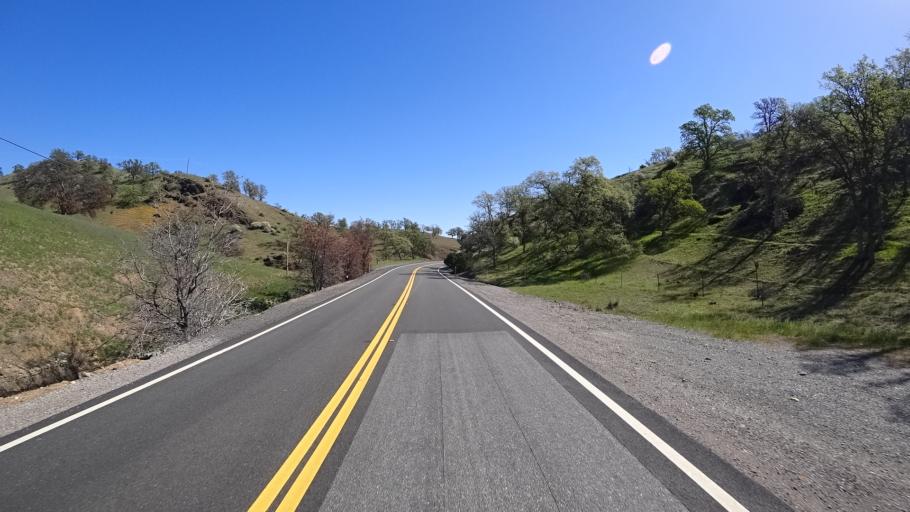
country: US
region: California
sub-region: Glenn County
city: Orland
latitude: 39.6550
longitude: -122.5810
